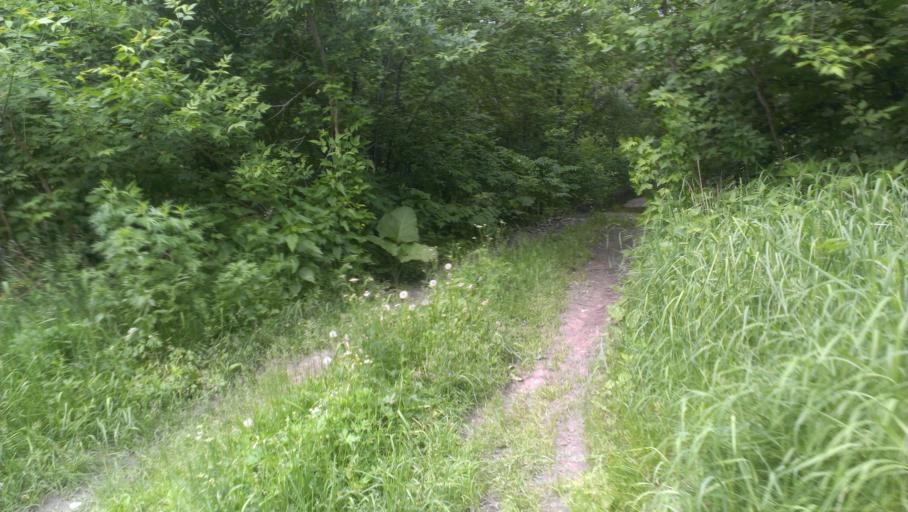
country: RU
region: Altai Krai
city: Sannikovo
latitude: 53.3419
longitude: 84.0589
